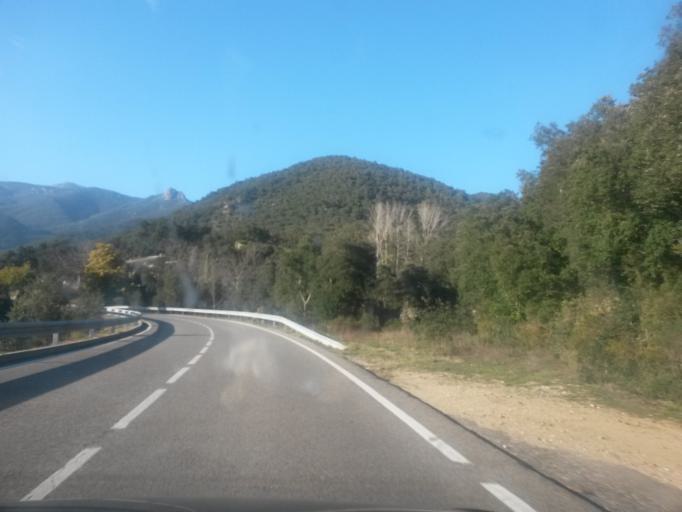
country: ES
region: Catalonia
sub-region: Provincia de Girona
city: Macanet de Cabrenys
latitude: 42.3853
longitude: 2.7863
